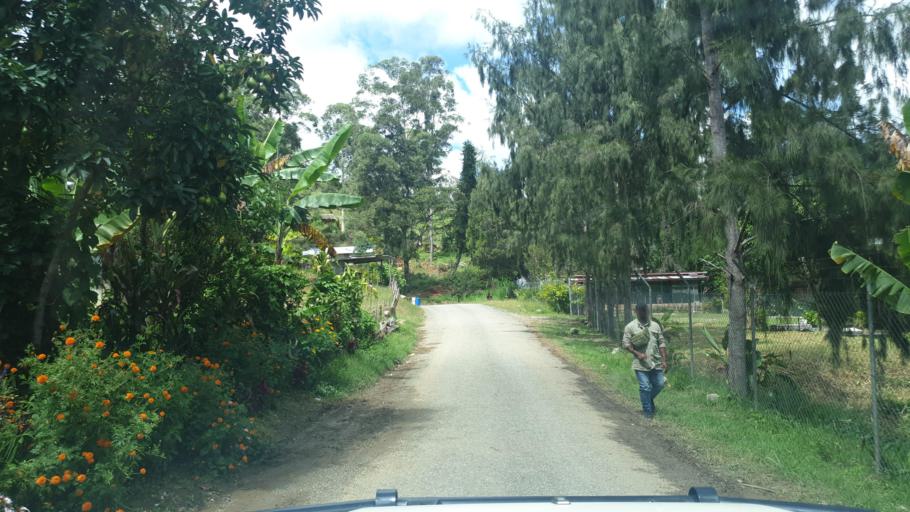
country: PG
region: Chimbu
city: Kundiawa
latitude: -6.1598
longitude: 145.1340
